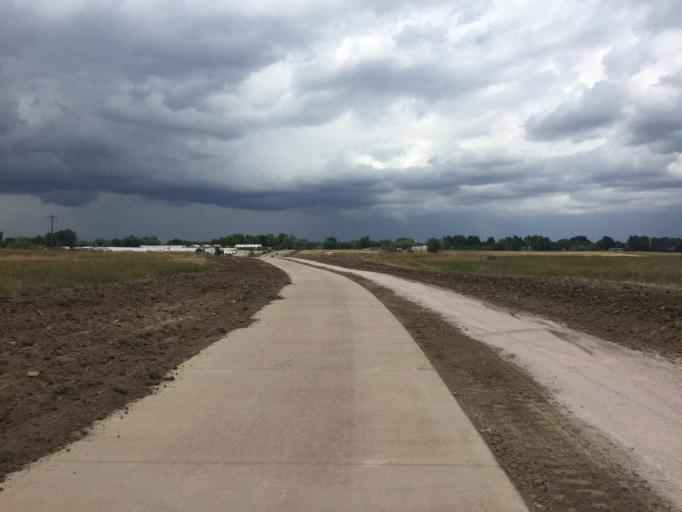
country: US
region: Colorado
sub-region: Larimer County
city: Fort Collins
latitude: 40.4958
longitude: -105.0956
